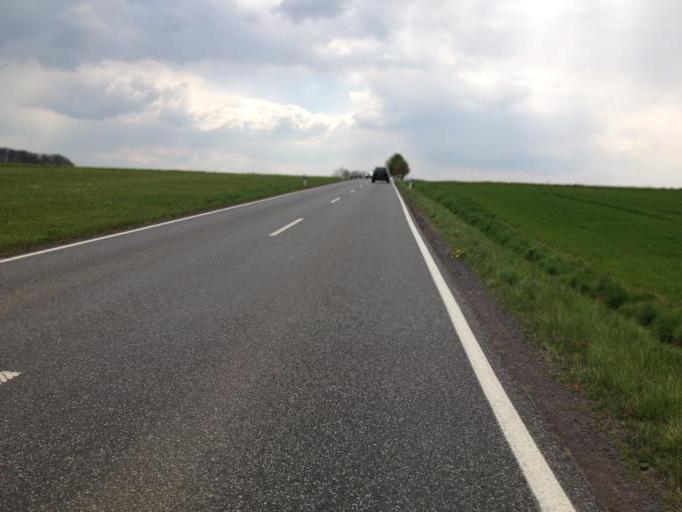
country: DE
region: Hesse
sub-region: Regierungsbezirk Giessen
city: Grunberg
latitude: 50.6200
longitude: 8.9825
